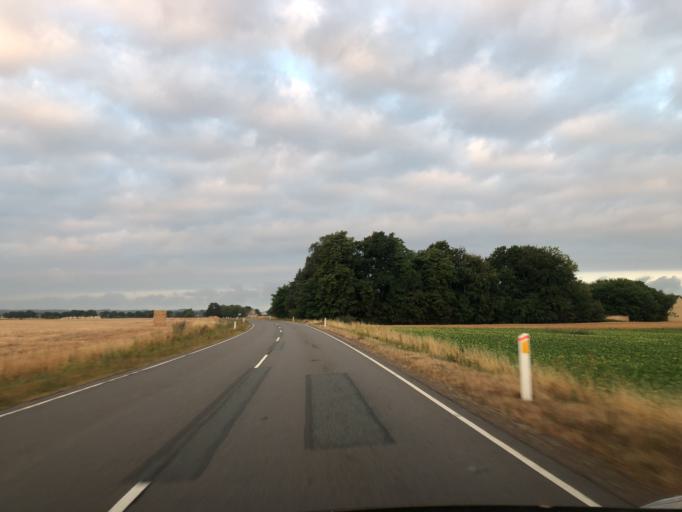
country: DK
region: Zealand
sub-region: Slagelse Kommune
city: Slagelse
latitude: 55.4519
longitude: 11.4337
